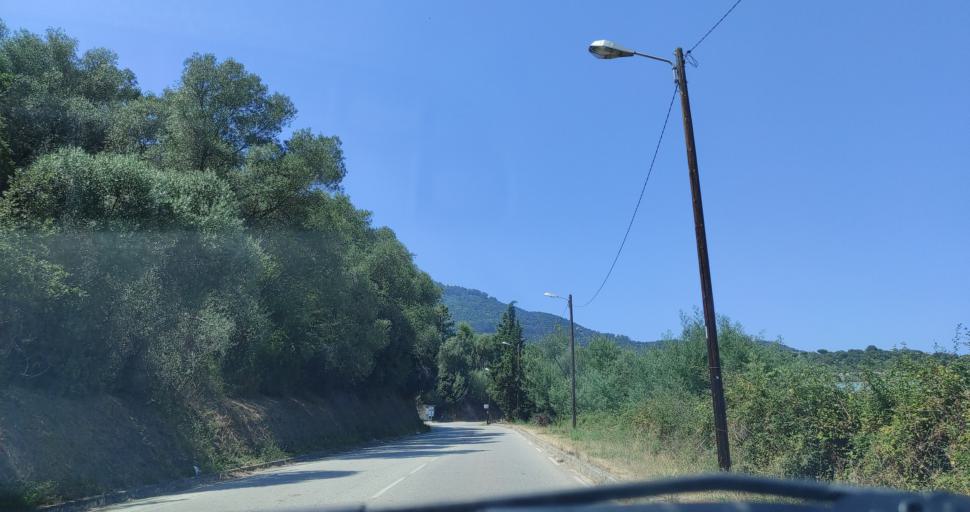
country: FR
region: Corsica
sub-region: Departement de la Corse-du-Sud
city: Ajaccio
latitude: 41.9406
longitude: 8.7371
